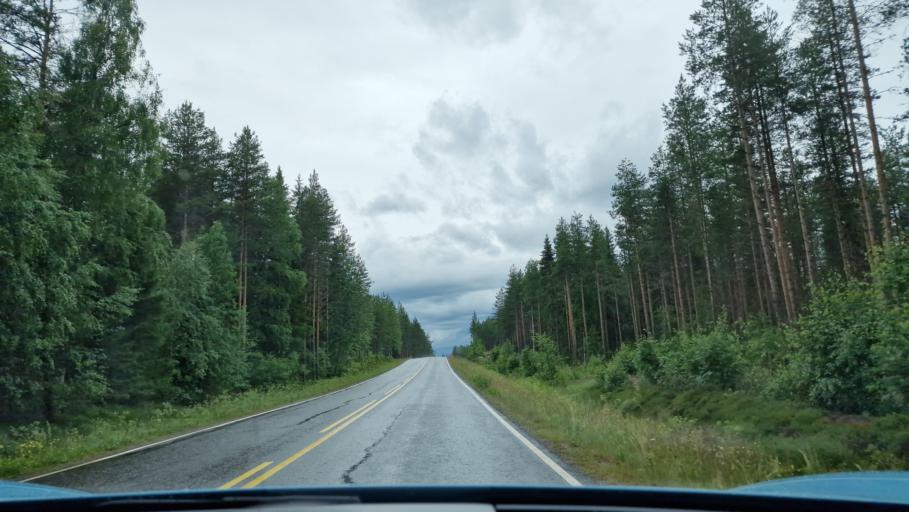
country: FI
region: Central Finland
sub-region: Saarijaervi-Viitasaari
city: Pylkoenmaeki
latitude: 62.6688
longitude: 24.5307
